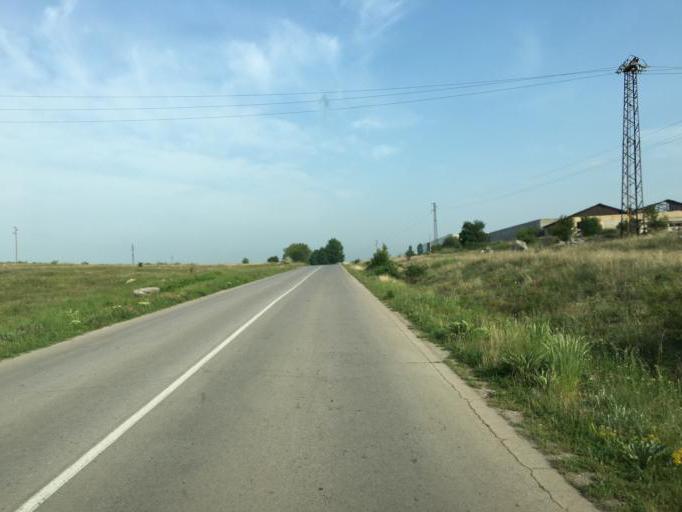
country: BG
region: Pernik
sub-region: Obshtina Radomir
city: Radomir
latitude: 42.4964
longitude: 23.0359
